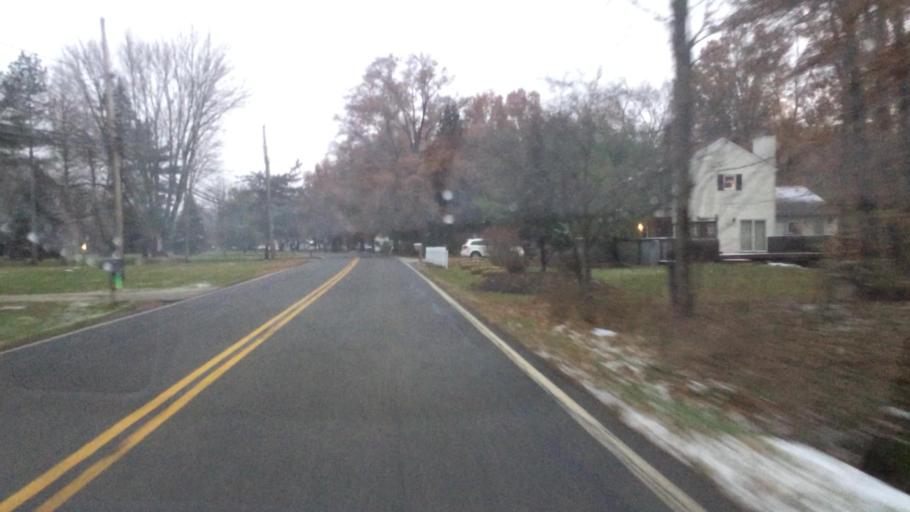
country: US
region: Ohio
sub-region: Cuyahoga County
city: Olmsted Falls
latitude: 41.3541
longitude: -81.9252
